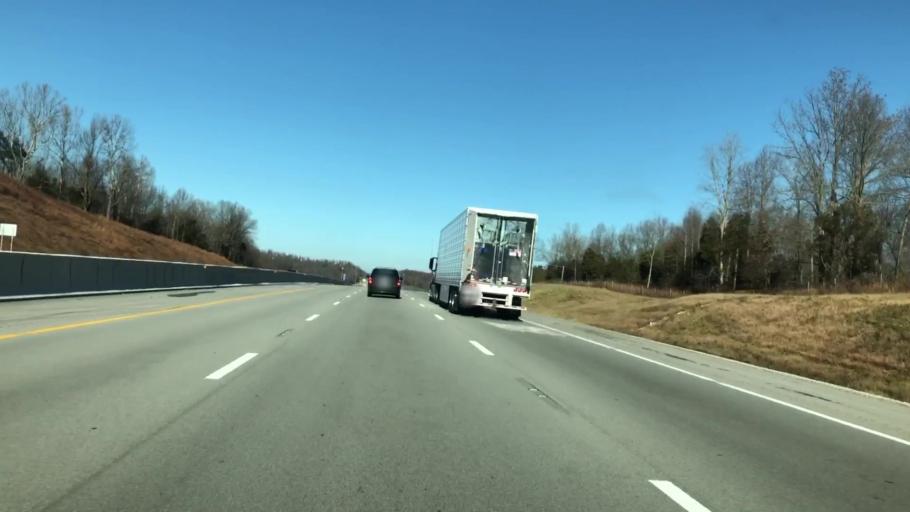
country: US
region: Kentucky
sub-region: Hart County
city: Munfordville
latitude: 37.3690
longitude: -85.8918
